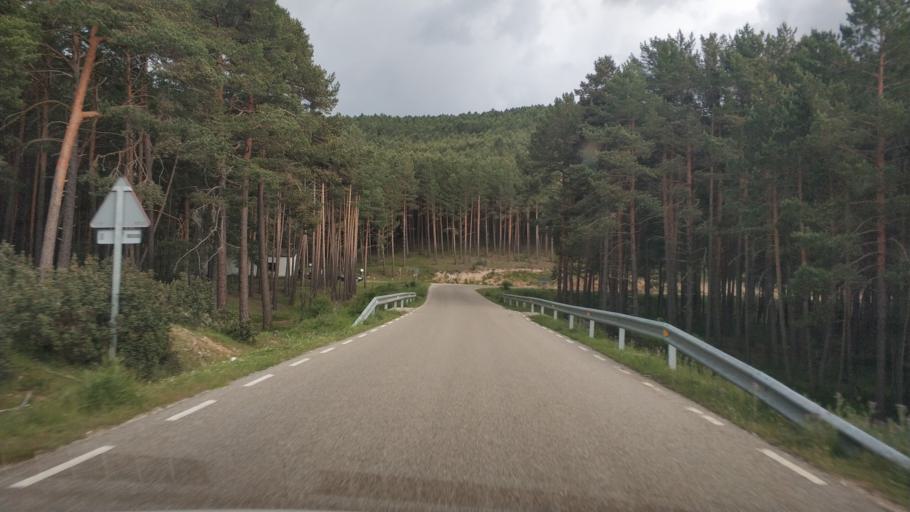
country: ES
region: Castille and Leon
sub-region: Provincia de Soria
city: San Leonardo de Yague
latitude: 41.8531
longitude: -3.0692
